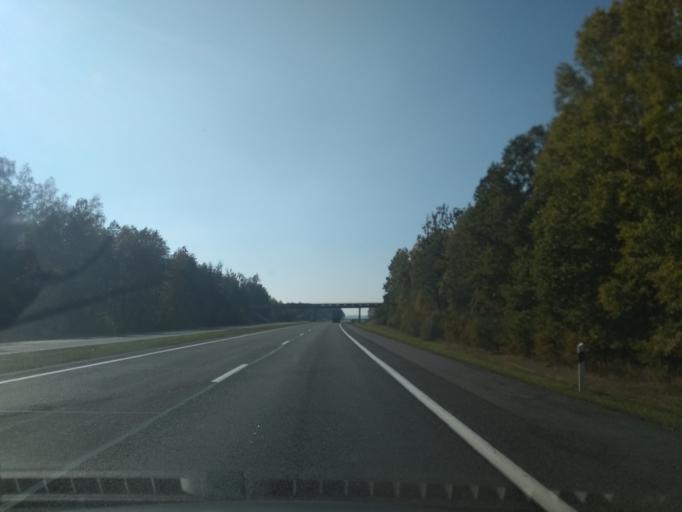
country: BY
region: Brest
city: Ivatsevichy
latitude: 52.6788
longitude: 25.3250
